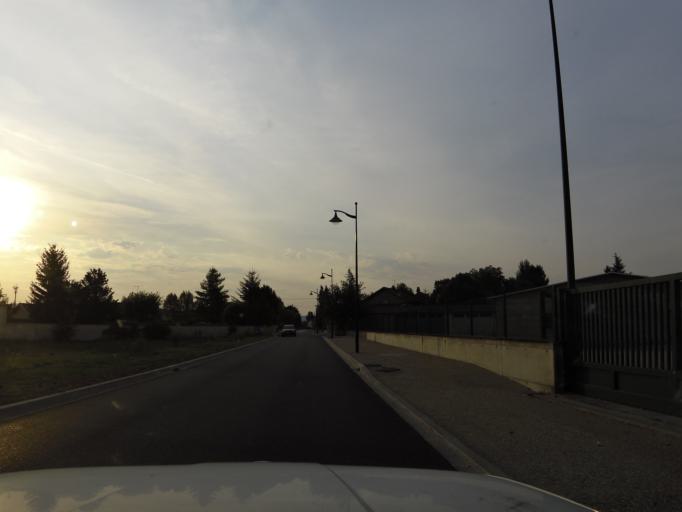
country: FR
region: Rhone-Alpes
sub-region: Departement de l'Ain
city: Saint-Maurice-de-Gourdans
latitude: 45.8192
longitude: 5.2068
